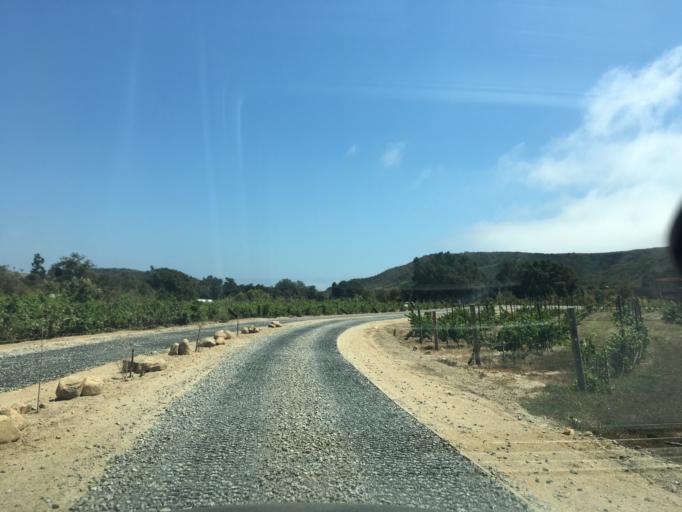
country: MX
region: Baja California
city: El Sauzal
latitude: 31.9444
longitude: -116.7375
